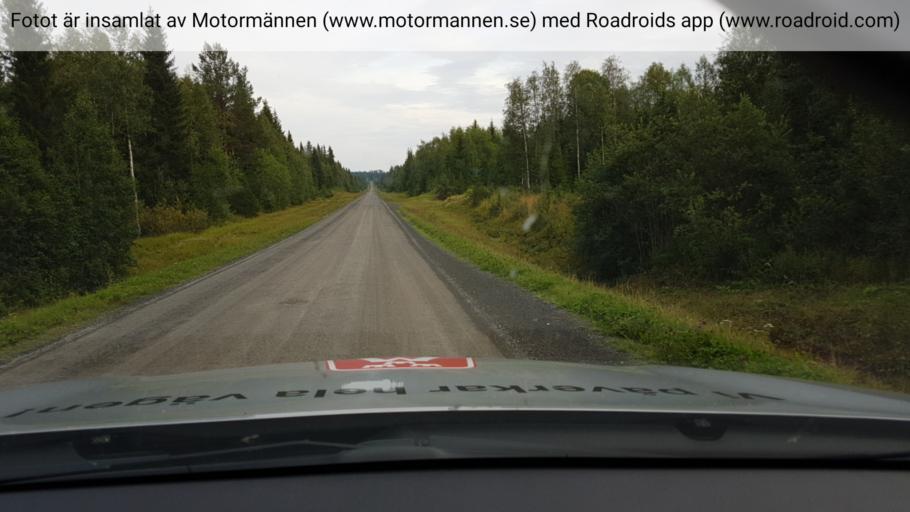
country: SE
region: Jaemtland
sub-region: OEstersunds Kommun
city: Lit
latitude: 63.6600
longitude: 14.9149
